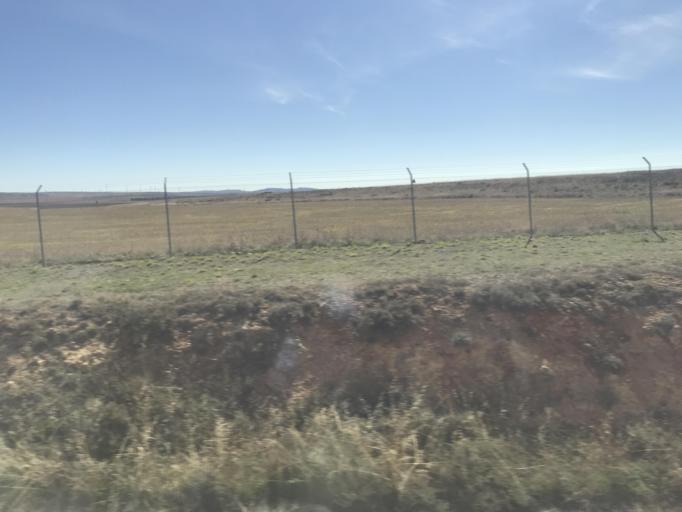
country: ES
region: Castille-La Mancha
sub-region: Provincia de Guadalajara
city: Anguita
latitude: 41.0989
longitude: -2.3837
